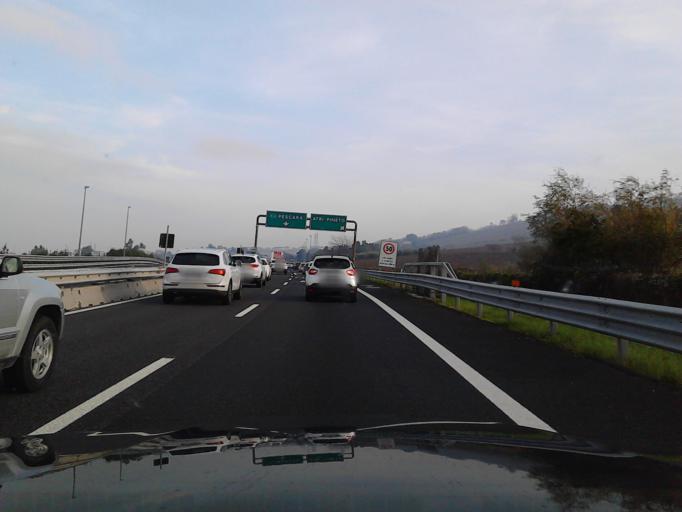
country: IT
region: Abruzzo
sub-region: Provincia di Teramo
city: Borgo Santa Maria Immacolata
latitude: 42.6079
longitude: 14.0425
